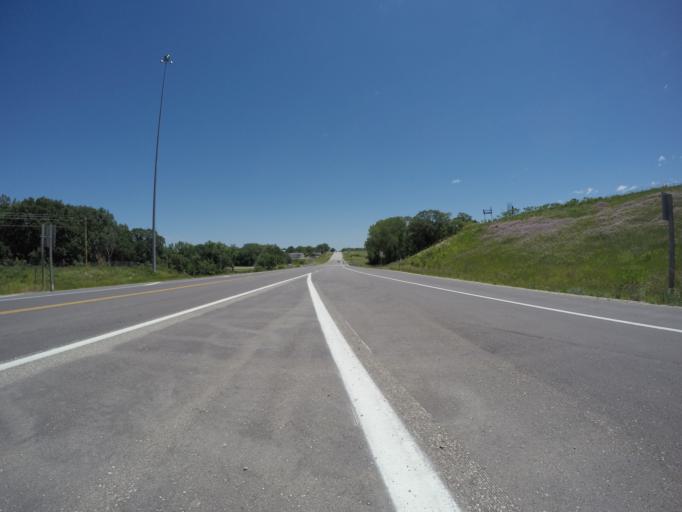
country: US
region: Kansas
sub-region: Republic County
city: Belleville
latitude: 39.8126
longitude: -97.6438
